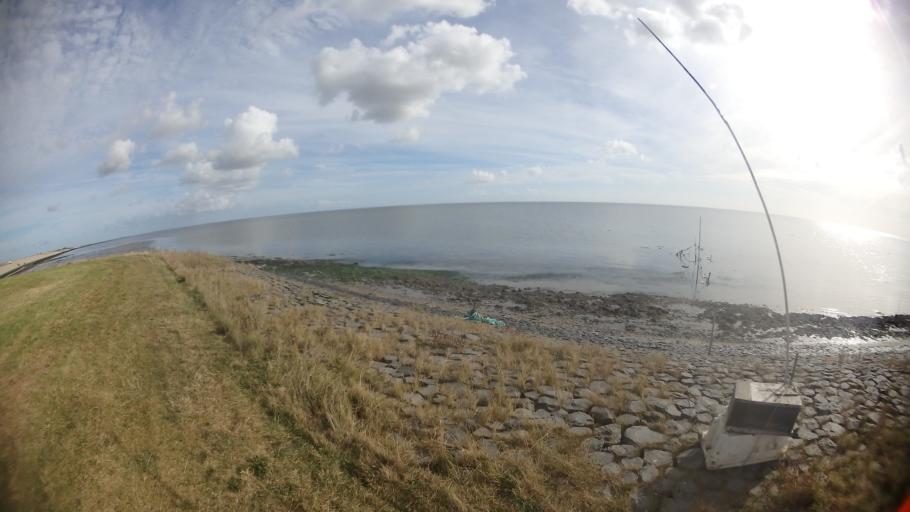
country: NL
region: North Holland
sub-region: Gemeente Texel
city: Den Burg
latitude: 53.0972
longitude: 4.8994
